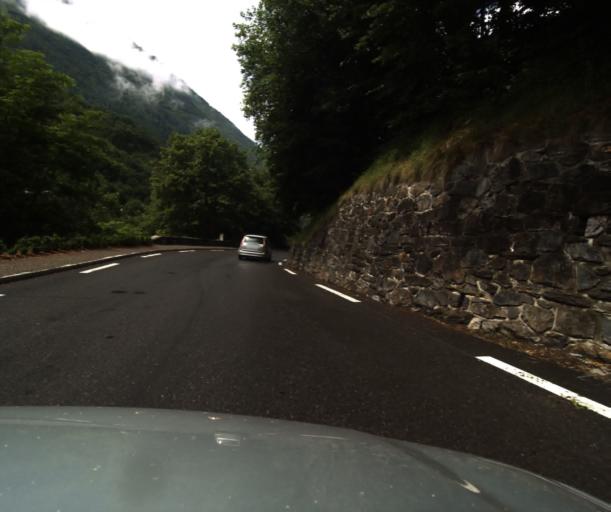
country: FR
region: Midi-Pyrenees
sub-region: Departement des Hautes-Pyrenees
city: Luz-Saint-Sauveur
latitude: 42.8600
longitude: -0.0051
